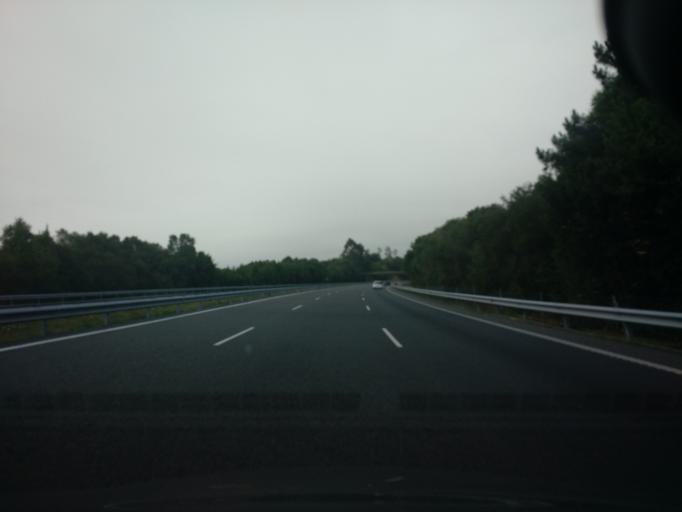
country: ES
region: Galicia
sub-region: Provincia da Coruna
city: Abegondo
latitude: 43.1757
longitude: -8.3122
